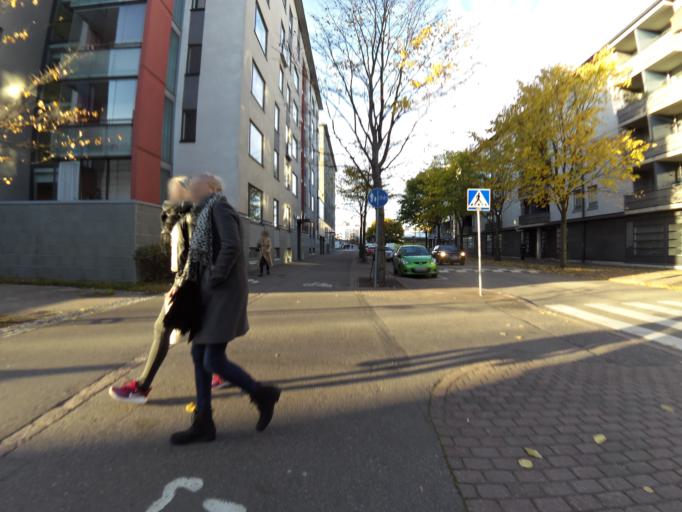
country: FI
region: Uusimaa
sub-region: Helsinki
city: Helsinki
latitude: 60.1922
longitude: 25.0317
